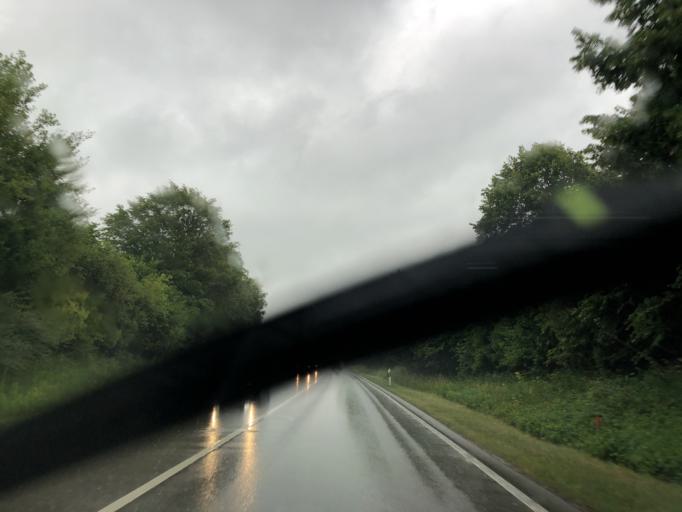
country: DE
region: Bavaria
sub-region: Upper Bavaria
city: Oberding
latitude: 48.3407
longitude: 11.8584
